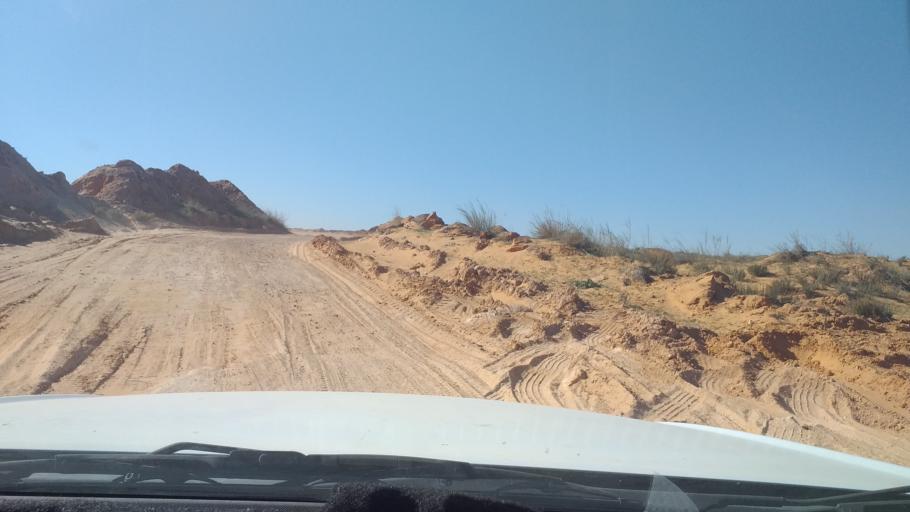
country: TN
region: Madanin
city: Medenine
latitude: 33.2634
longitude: 10.5785
